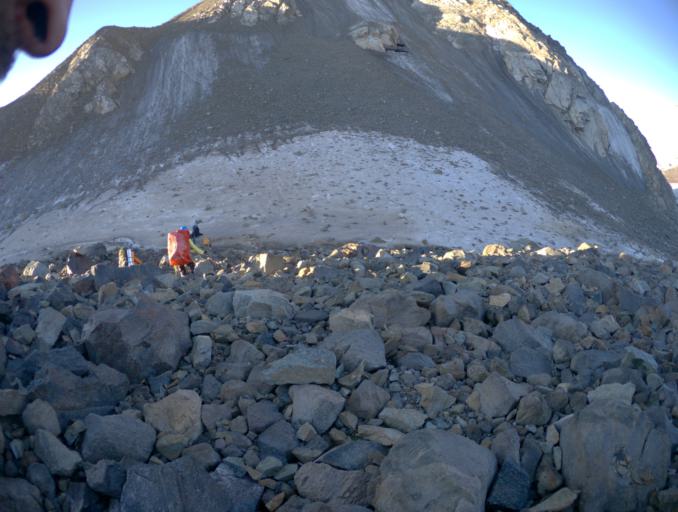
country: RU
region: Kabardino-Balkariya
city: Terskol
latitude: 43.3138
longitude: 42.5168
